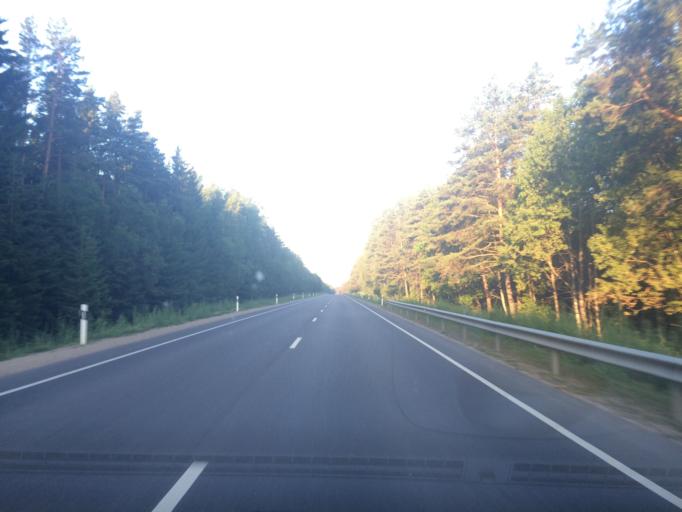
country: LT
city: Zarasai
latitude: 55.6877
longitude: 26.1326
